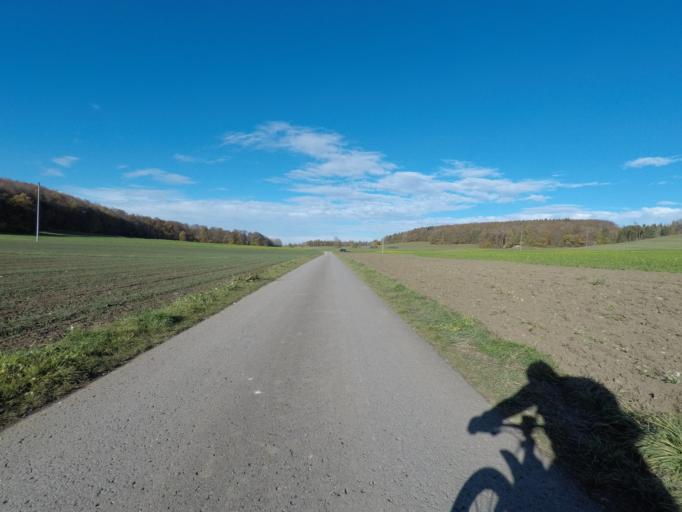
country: DE
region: Baden-Wuerttemberg
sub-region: Tuebingen Region
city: Pfullingen
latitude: 48.4141
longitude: 9.2117
